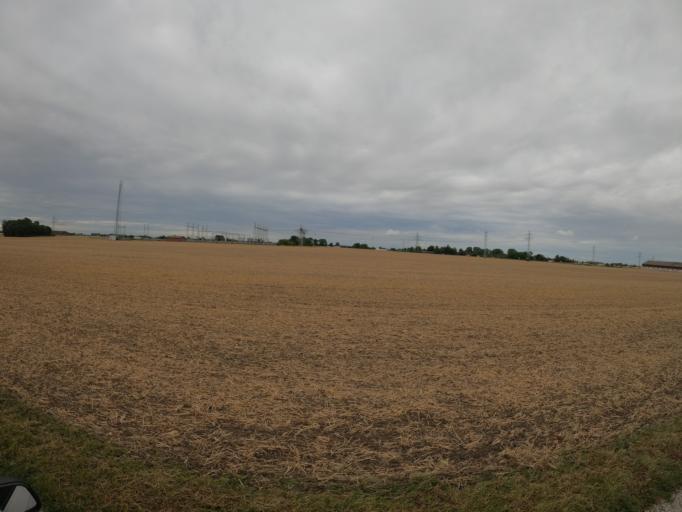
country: SE
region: Skane
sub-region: Lunds Kommun
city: Lund
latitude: 55.7420
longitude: 13.1493
